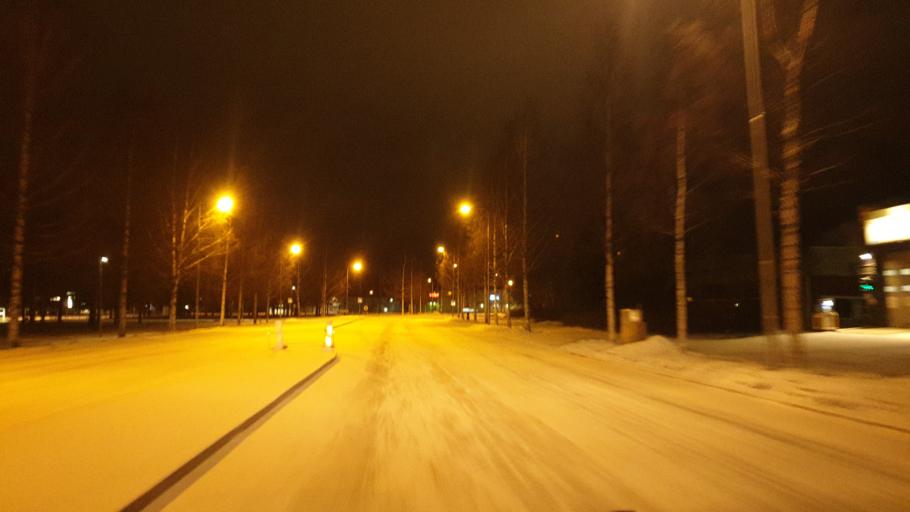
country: FI
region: Northern Ostrobothnia
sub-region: Oulu
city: Oulu
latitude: 64.9962
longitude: 25.4573
